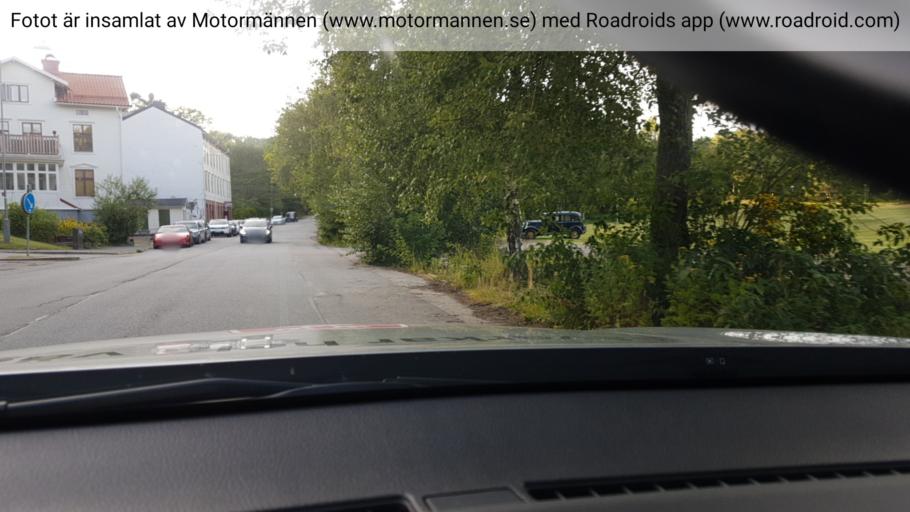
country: SE
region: Vaestra Goetaland
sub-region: Goteborg
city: Majorna
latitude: 57.6947
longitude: 11.9020
